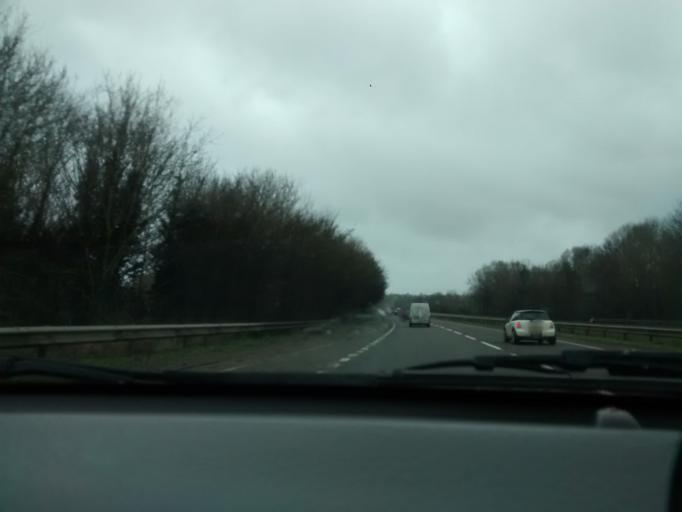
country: GB
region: England
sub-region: Suffolk
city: Bramford
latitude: 52.1096
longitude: 1.1060
